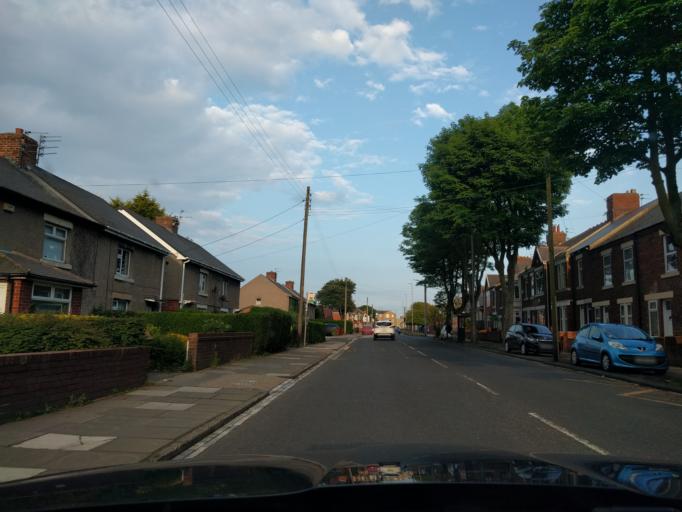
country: GB
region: England
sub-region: Northumberland
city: Bedlington
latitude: 55.1326
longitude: -1.6039
